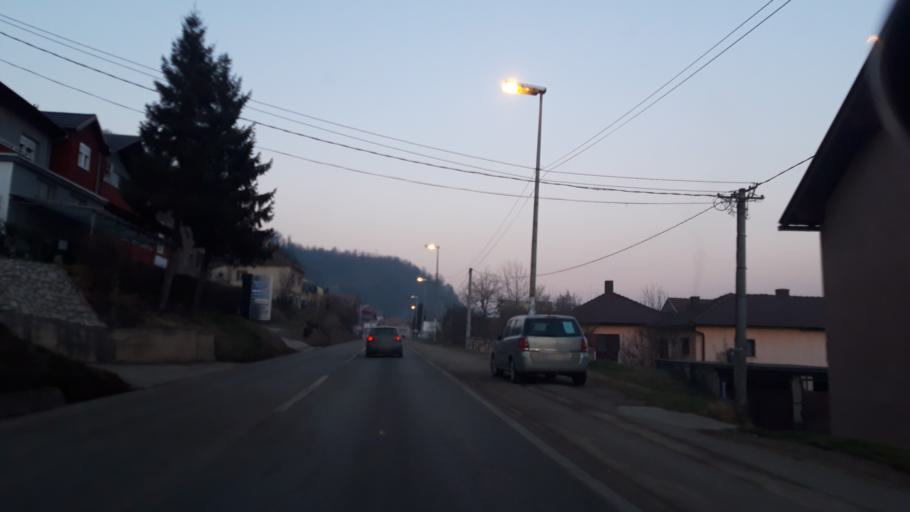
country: BA
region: Republika Srpska
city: Zvornik
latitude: 44.4032
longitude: 19.1163
